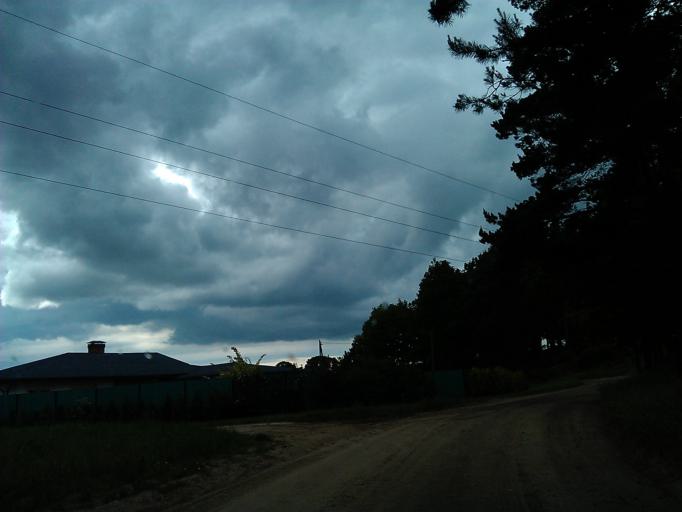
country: LV
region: Adazi
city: Adazi
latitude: 57.0825
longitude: 24.3062
